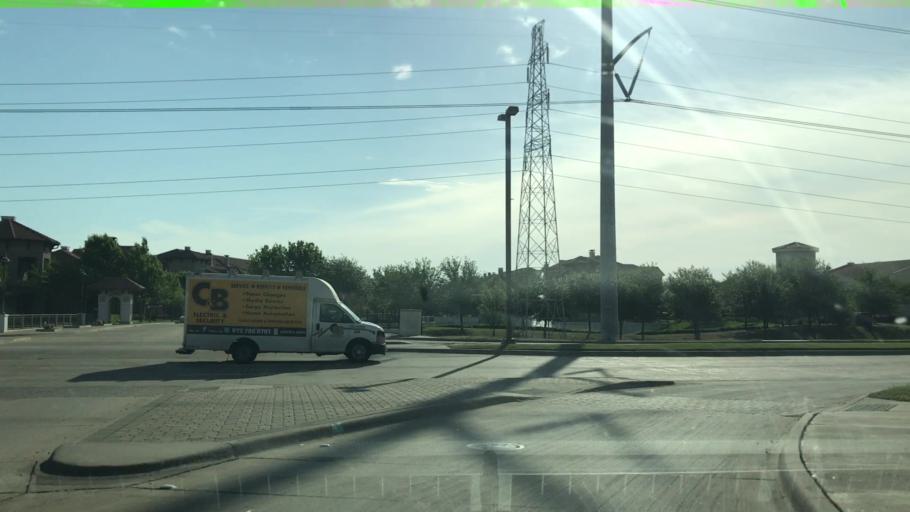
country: US
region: Texas
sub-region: Dallas County
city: Farmers Branch
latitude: 32.8994
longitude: -96.9402
